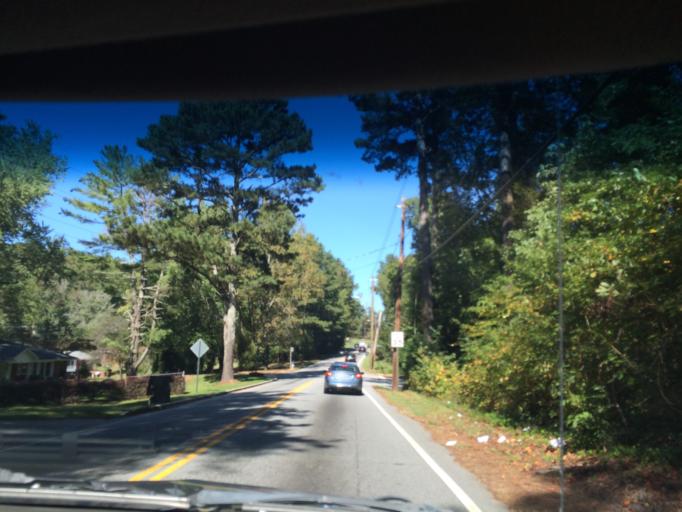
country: US
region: Georgia
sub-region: Fulton County
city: College Park
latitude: 33.6561
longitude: -84.4824
